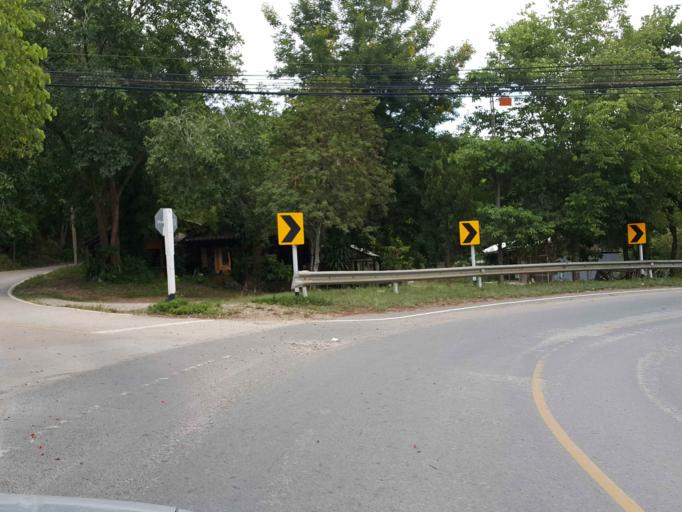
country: TH
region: Chiang Mai
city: Hang Dong
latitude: 18.7523
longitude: 98.8890
